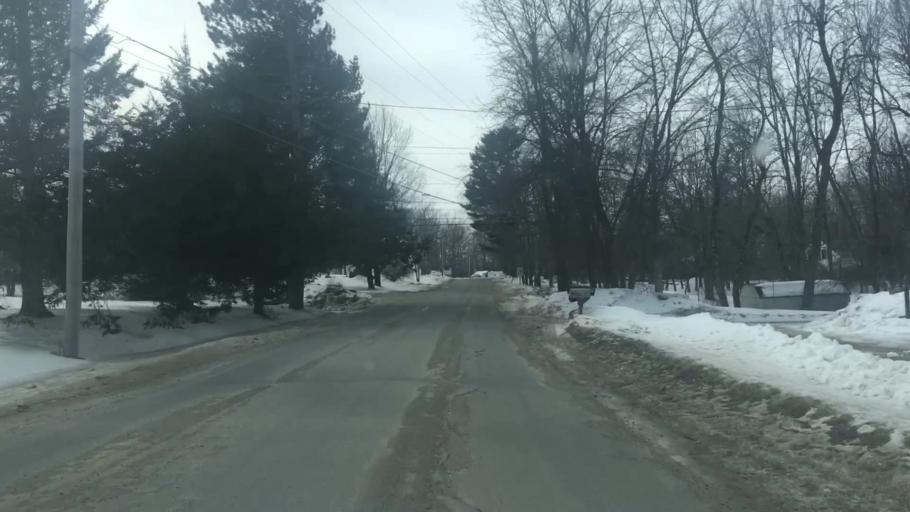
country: US
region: Maine
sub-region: Hancock County
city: Orland
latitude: 44.5711
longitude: -68.7351
